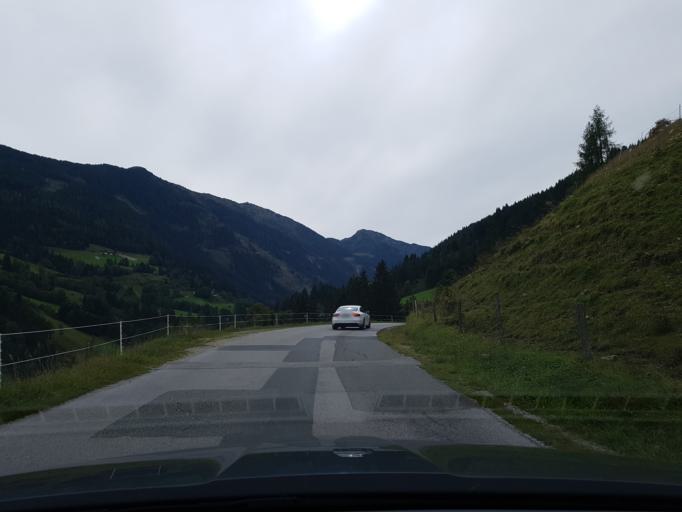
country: AT
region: Salzburg
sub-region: Politischer Bezirk Sankt Johann im Pongau
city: Forstau
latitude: 47.3681
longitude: 13.5538
